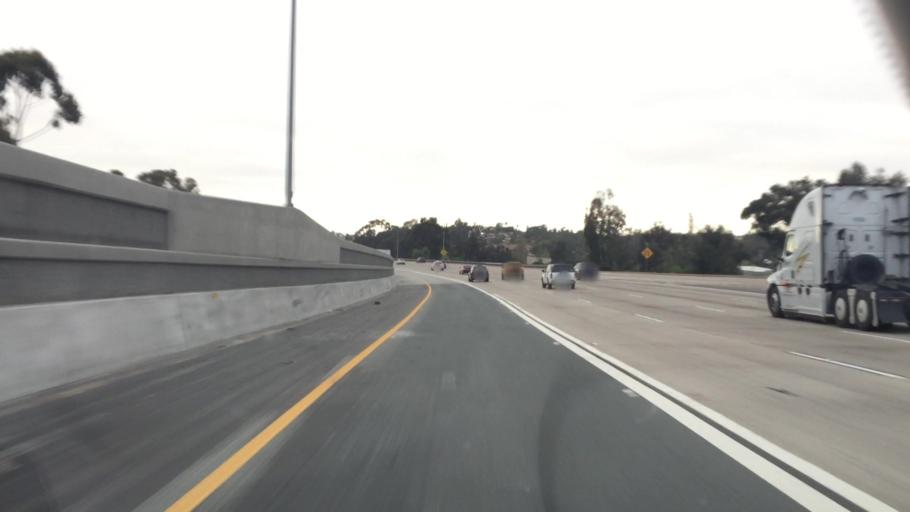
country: US
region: California
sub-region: San Diego County
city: Chula Vista
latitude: 32.6449
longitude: -117.0583
